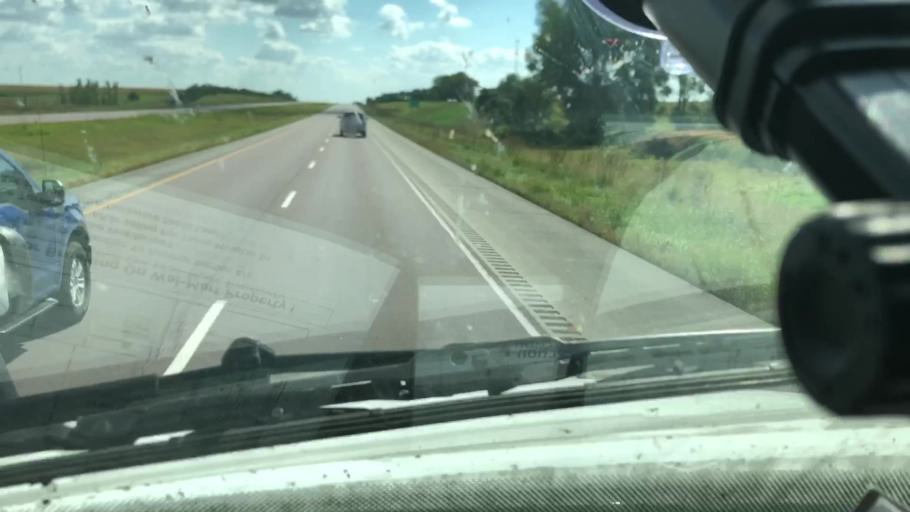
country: US
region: Iowa
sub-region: Worth County
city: Manly
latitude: 43.3023
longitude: -93.3497
